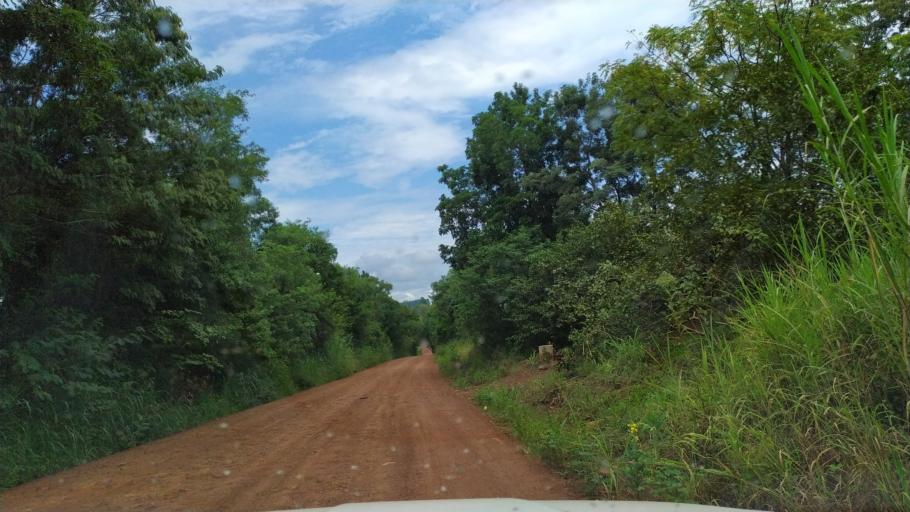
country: AR
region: Misiones
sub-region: Departamento de Eldorado
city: Eldorado
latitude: -26.4280
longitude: -54.6047
